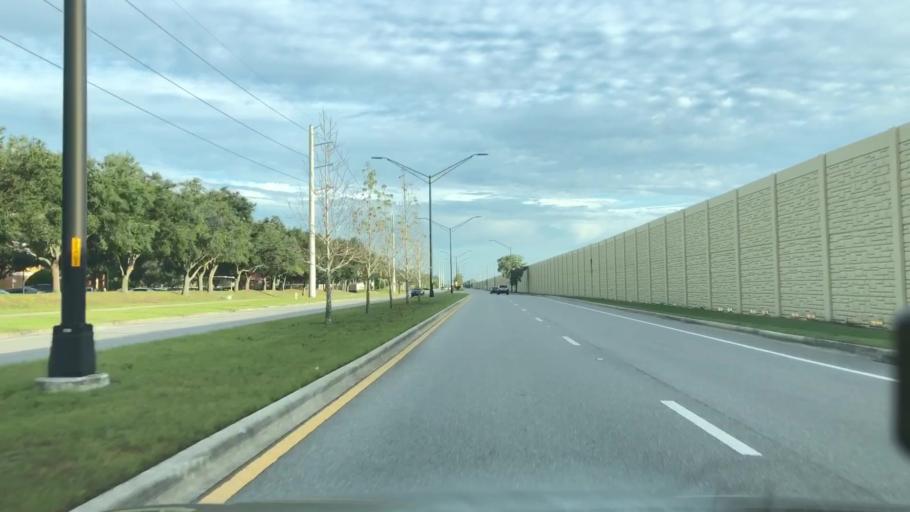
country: US
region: Florida
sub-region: Sarasota County
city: Fruitville
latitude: 27.3462
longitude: -82.4473
